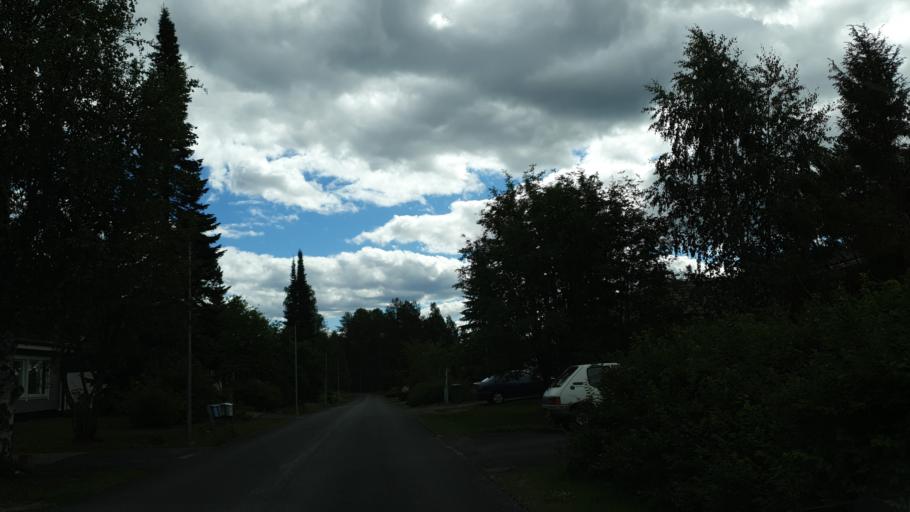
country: FI
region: Kainuu
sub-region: Kehys-Kainuu
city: Kuhmo
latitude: 64.1169
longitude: 29.5039
